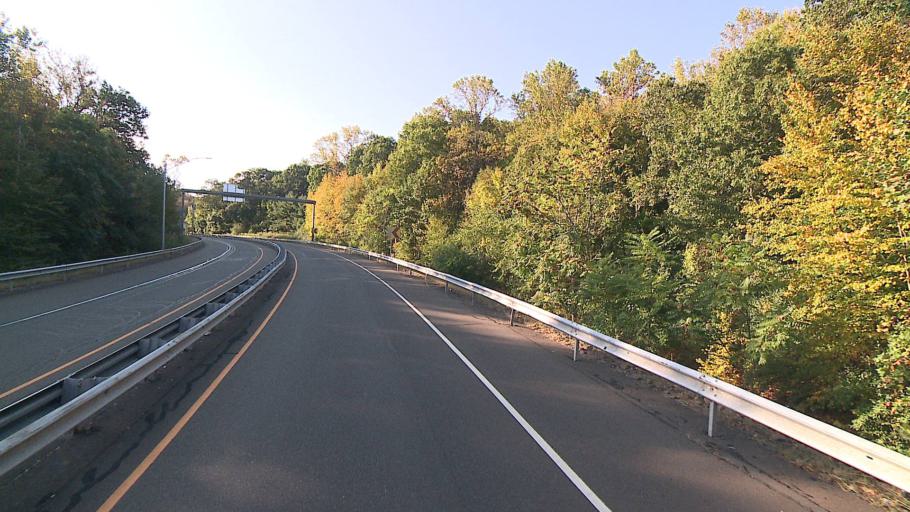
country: US
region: Connecticut
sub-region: New Haven County
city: City of Milford (balance)
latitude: 41.2487
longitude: -73.0863
